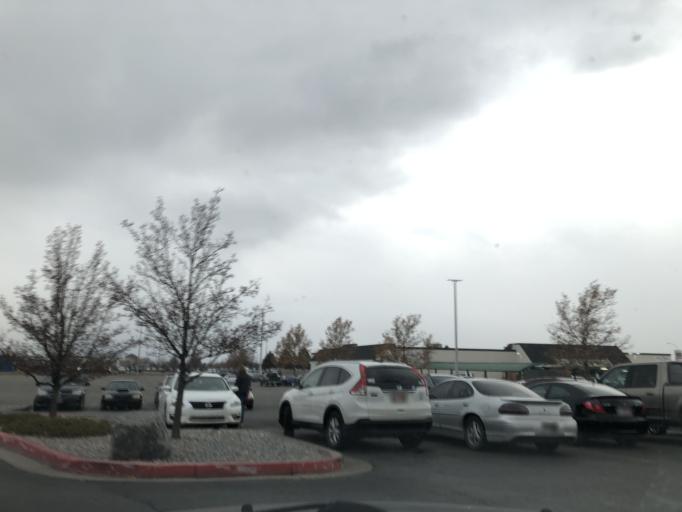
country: US
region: Utah
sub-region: Cache County
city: Logan
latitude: 41.7558
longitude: -111.8326
